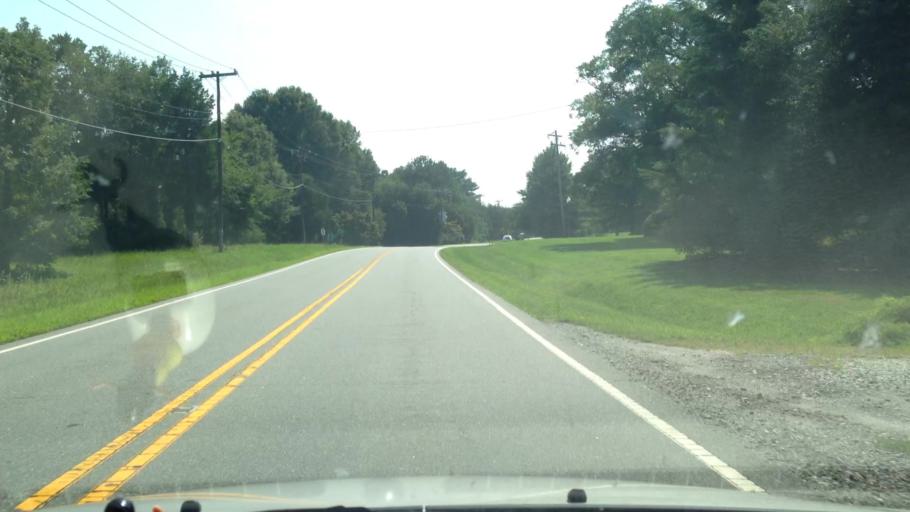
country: US
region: North Carolina
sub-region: Guilford County
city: Oak Ridge
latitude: 36.1639
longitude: -80.0038
